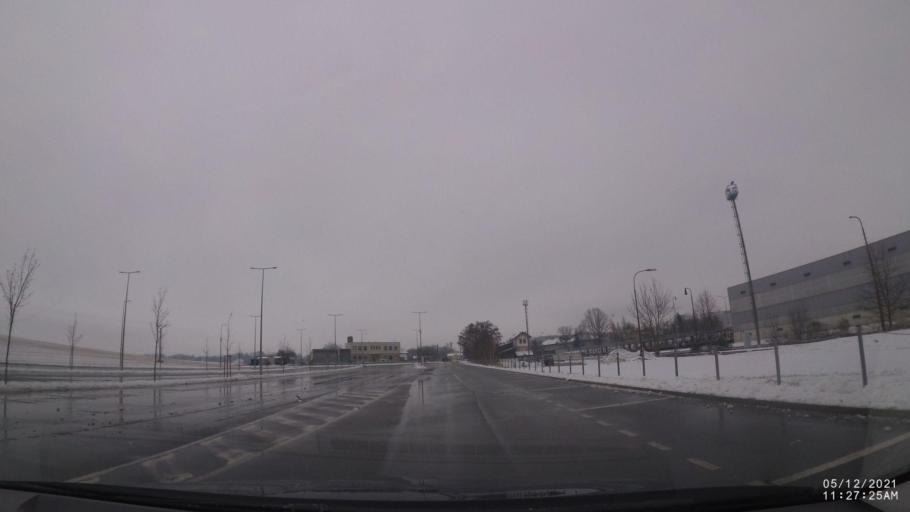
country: CZ
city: Kvasiny
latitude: 50.2007
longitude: 16.2552
